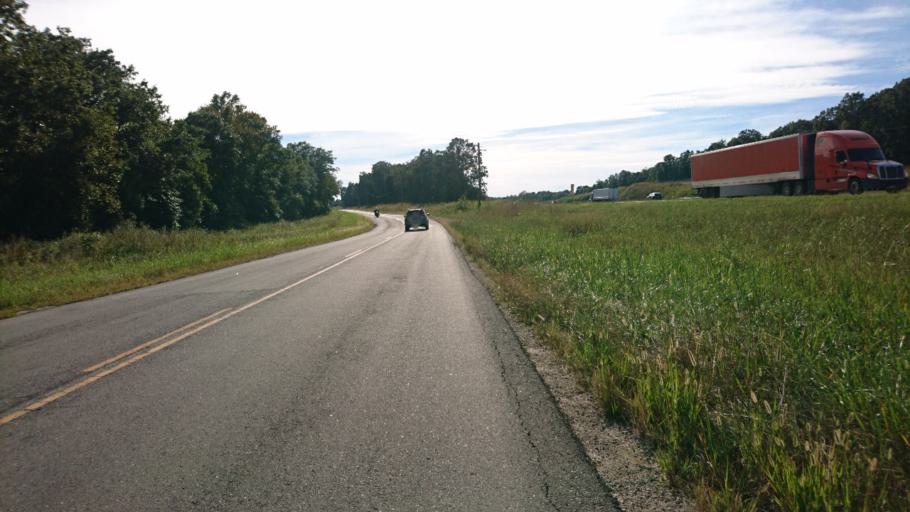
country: US
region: Missouri
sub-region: Crawford County
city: Cuba
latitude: 38.1078
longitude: -91.3396
